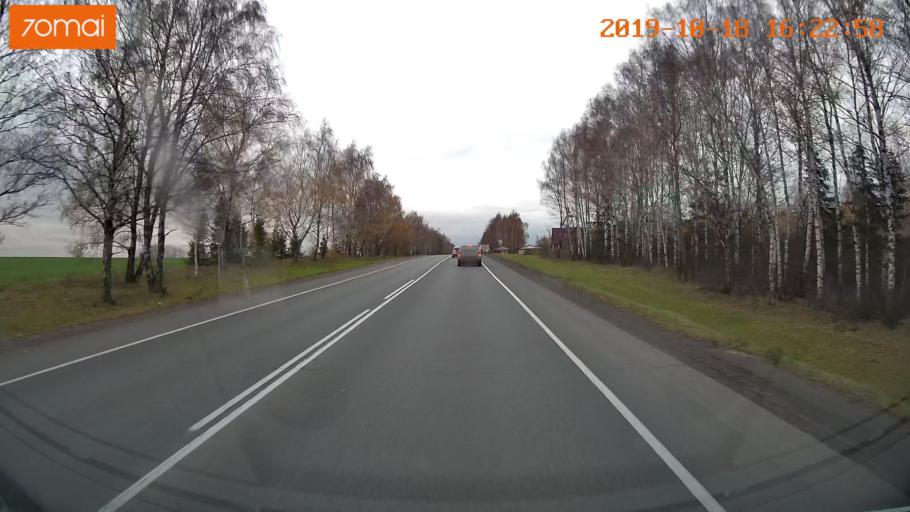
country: RU
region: Vladimir
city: Bogolyubovo
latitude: 56.2481
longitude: 40.4569
